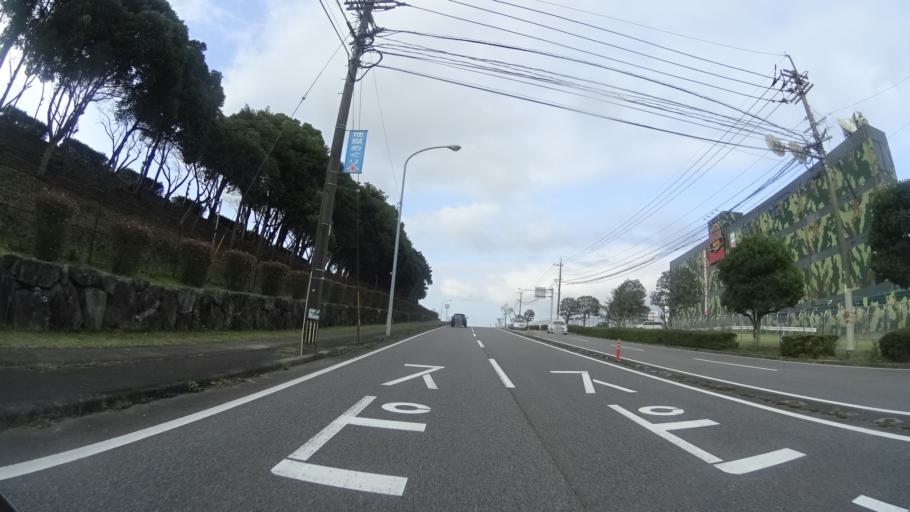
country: JP
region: Oita
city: Beppu
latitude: 33.2943
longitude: 131.4604
